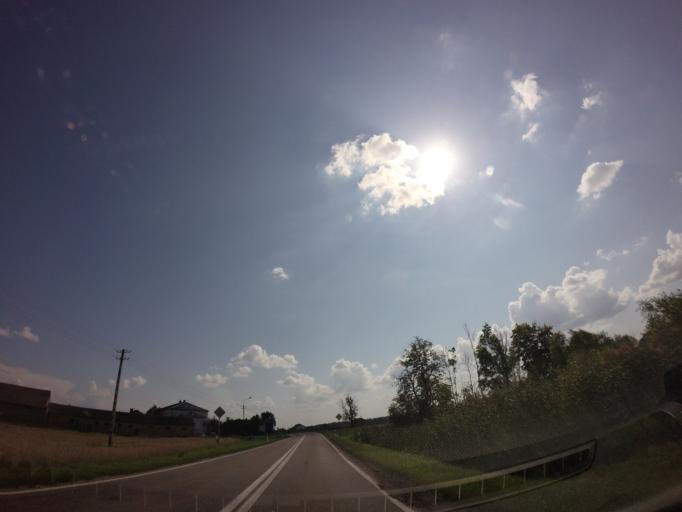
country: PL
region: Podlasie
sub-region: Powiat zambrowski
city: Zambrow
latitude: 52.9126
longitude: 22.2556
